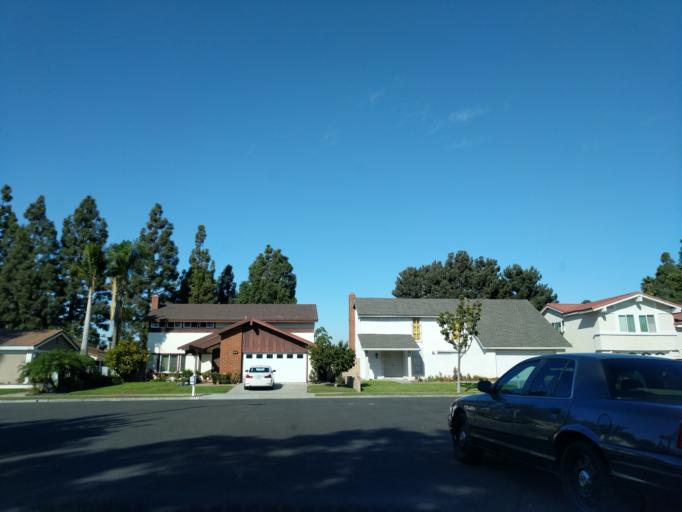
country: US
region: California
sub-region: Orange County
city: Irvine
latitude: 33.6739
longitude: -117.8220
